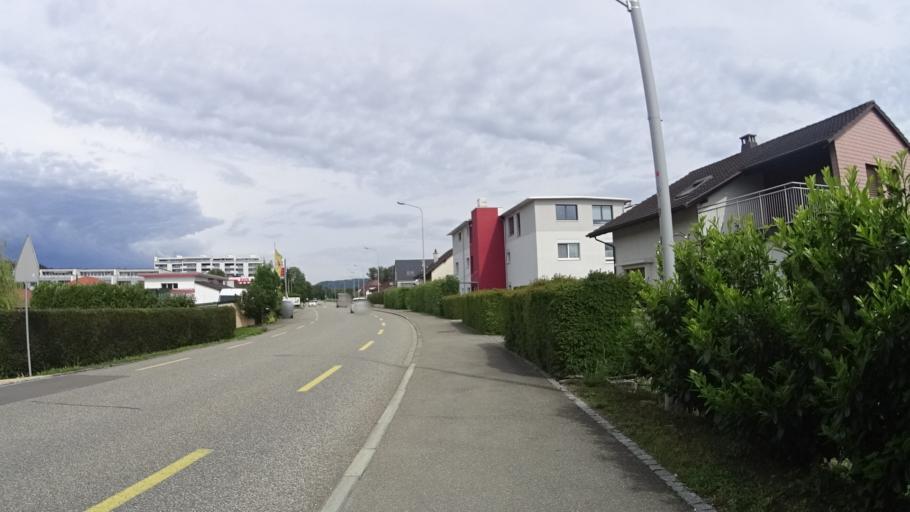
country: CH
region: Aargau
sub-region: Bezirk Laufenburg
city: Eiken
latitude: 47.5531
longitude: 7.9905
